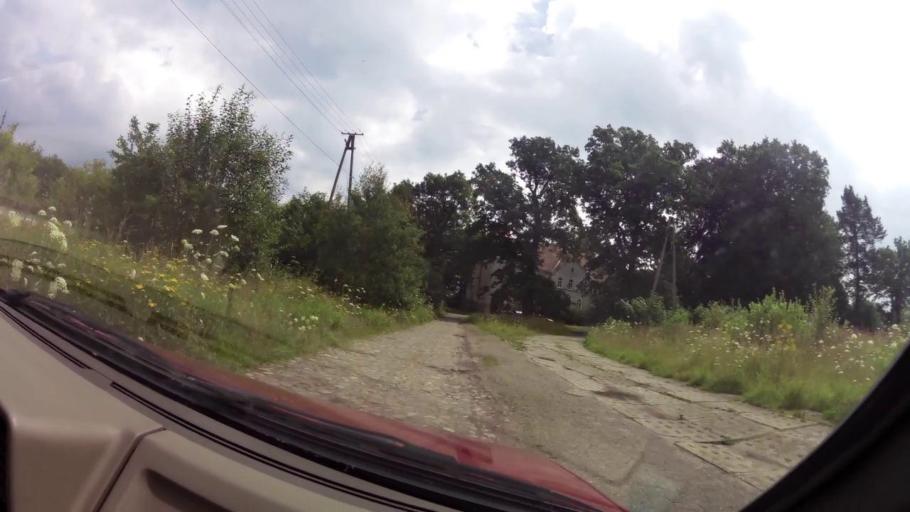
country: PL
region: West Pomeranian Voivodeship
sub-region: Powiat swidwinski
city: Polczyn-Zdroj
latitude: 53.7946
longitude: 16.0441
